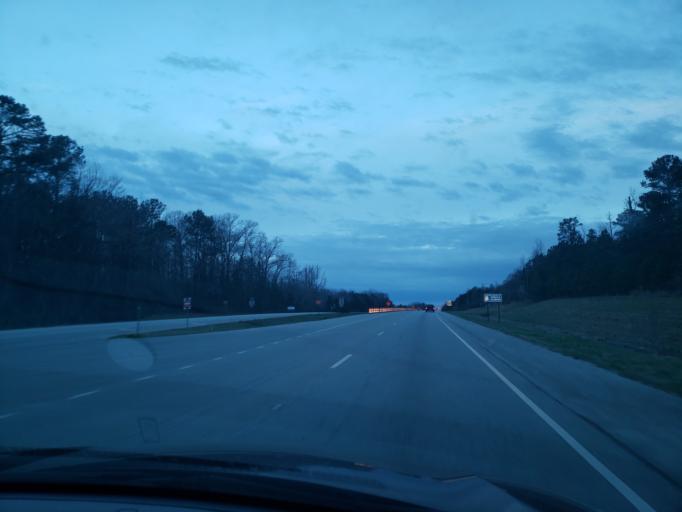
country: US
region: Alabama
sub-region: Lee County
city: Auburn
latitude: 32.6650
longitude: -85.4728
